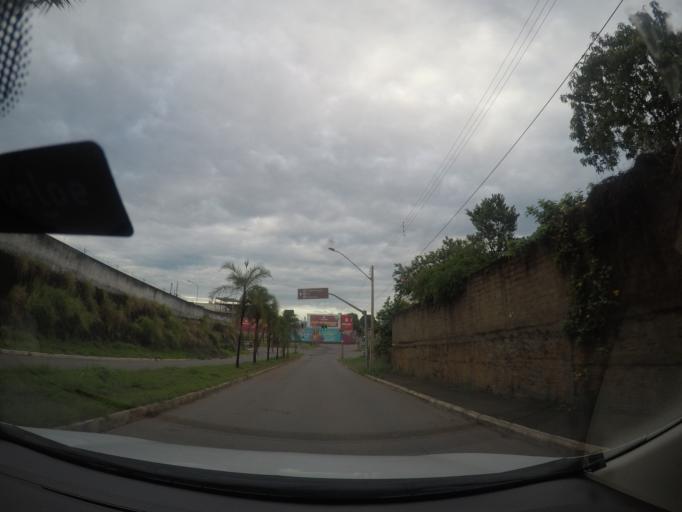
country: BR
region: Goias
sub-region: Goiania
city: Goiania
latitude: -16.6605
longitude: -49.2523
